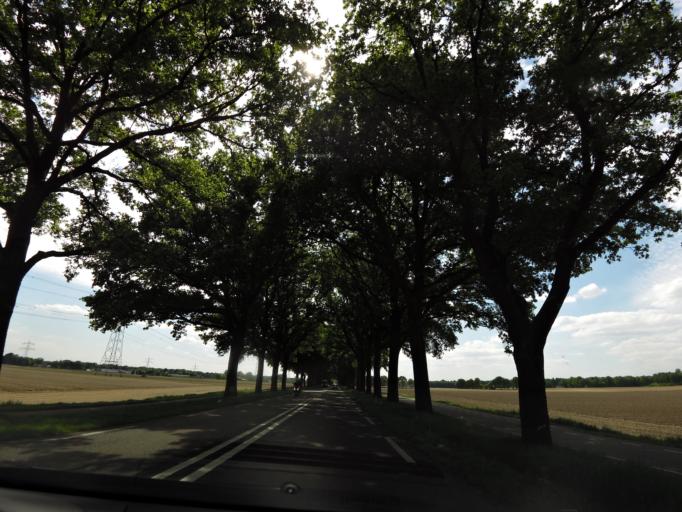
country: NL
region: Limburg
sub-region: Gemeente Leudal
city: Haelen
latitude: 51.2202
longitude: 5.9355
